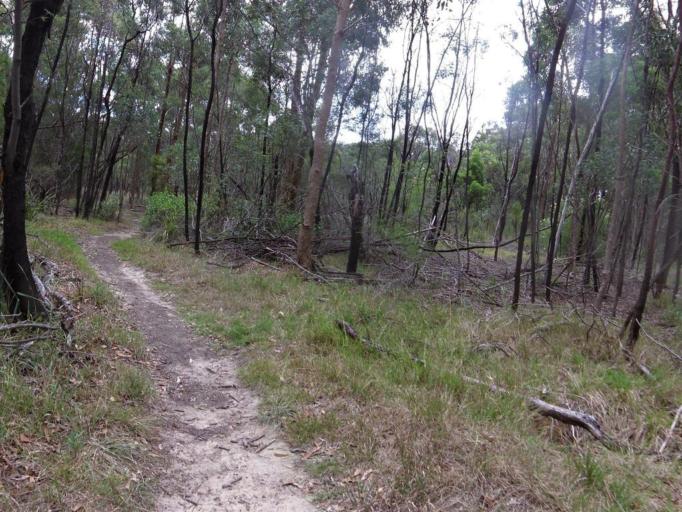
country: AU
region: Victoria
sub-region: Whitehorse
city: Forest Hill
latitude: -37.8271
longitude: 145.1634
